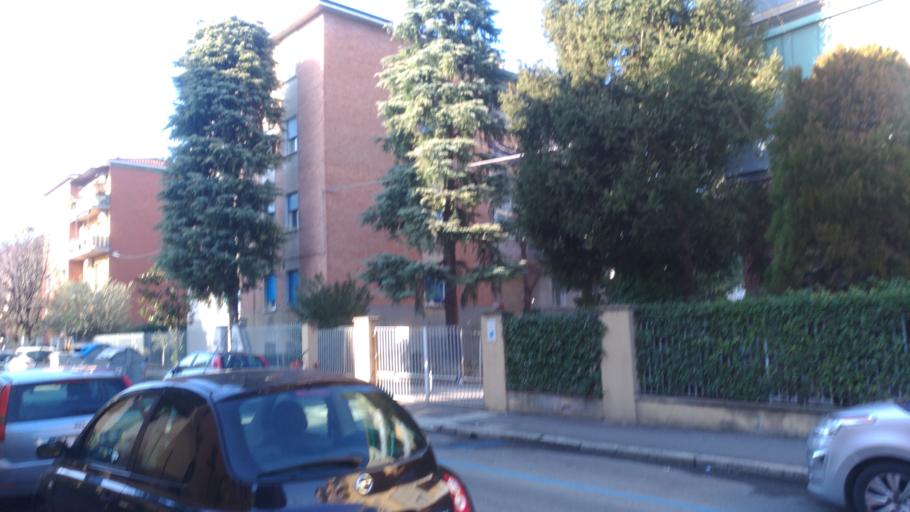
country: IT
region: Emilia-Romagna
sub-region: Provincia di Bologna
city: Bologna
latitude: 44.5248
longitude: 11.3484
